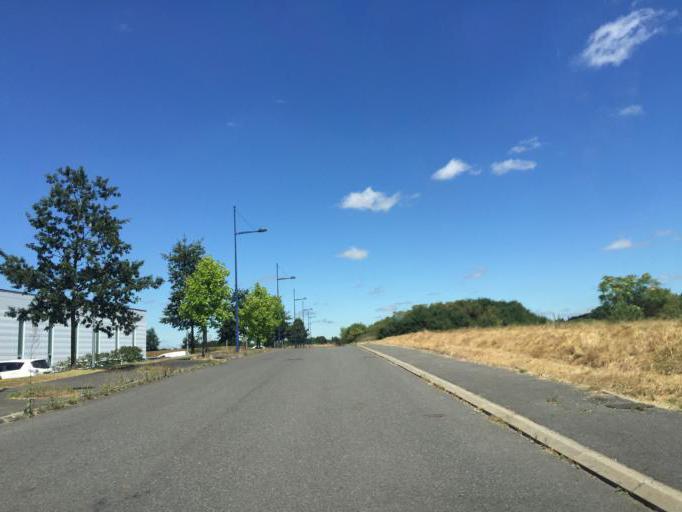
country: FR
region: Auvergne
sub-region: Departement de l'Allier
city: Avermes
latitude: 46.5946
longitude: 3.3287
